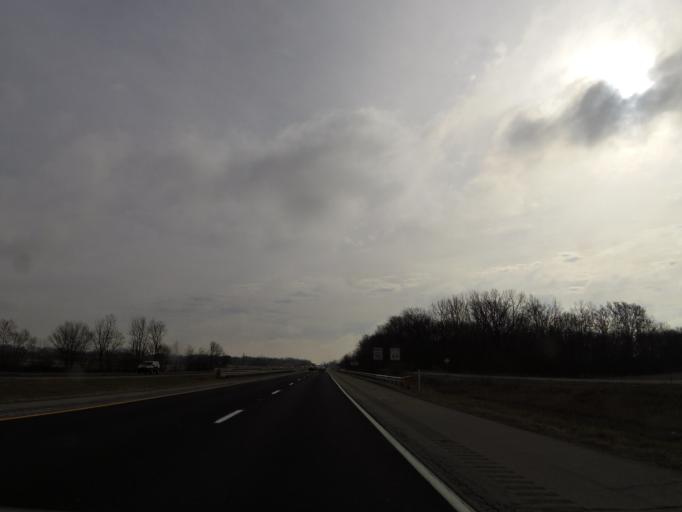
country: US
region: Indiana
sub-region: Hancock County
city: New Palestine
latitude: 39.6566
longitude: -85.9320
